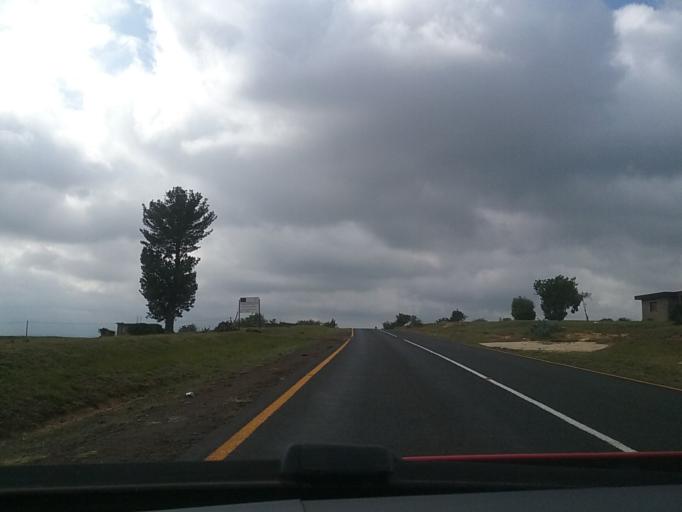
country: LS
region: Berea
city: Teyateyaneng
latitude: -29.1944
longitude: 27.8094
